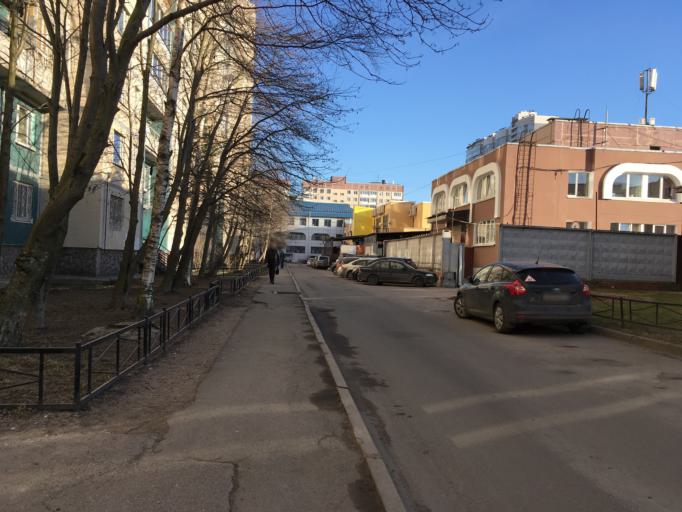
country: RU
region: St.-Petersburg
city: Staraya Derevnya
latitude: 60.0125
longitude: 30.2454
